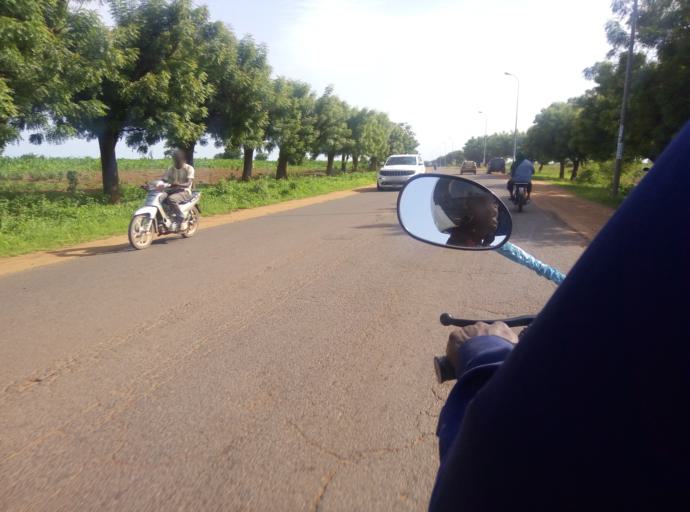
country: ML
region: Bamako
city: Bamako
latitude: 12.5536
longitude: -7.9477
